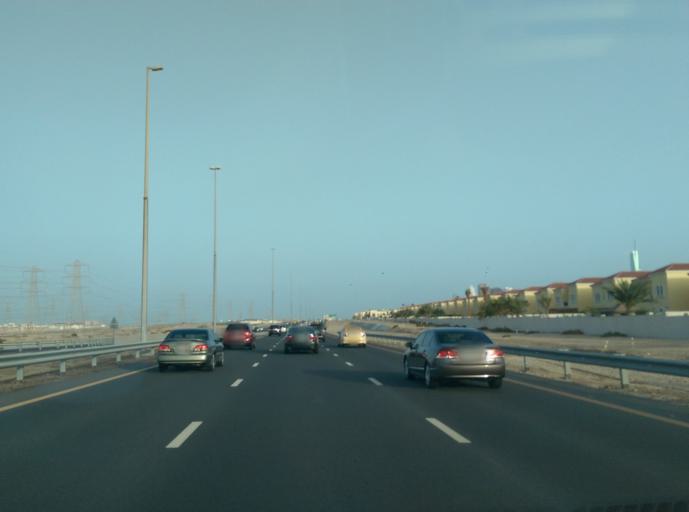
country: AE
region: Dubai
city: Dubai
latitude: 25.0435
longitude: 55.1529
